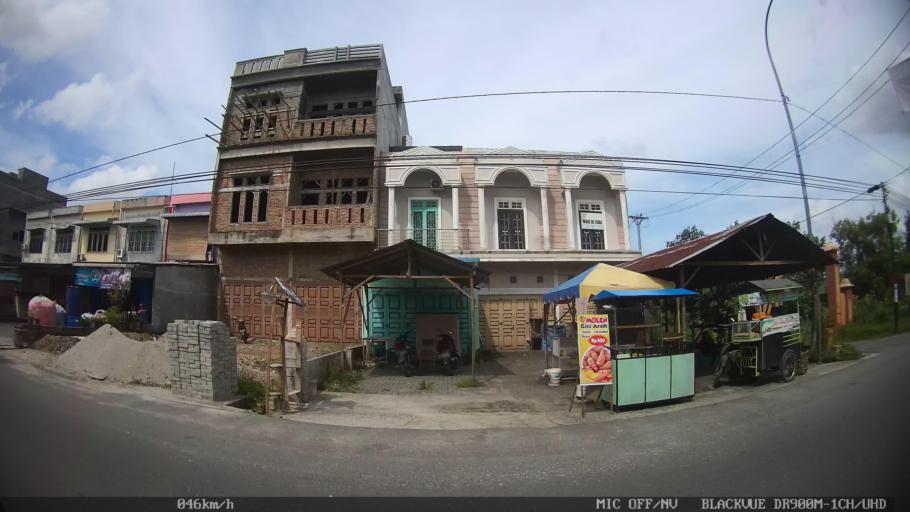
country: ID
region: North Sumatra
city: Percut
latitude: 3.5739
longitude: 98.8683
